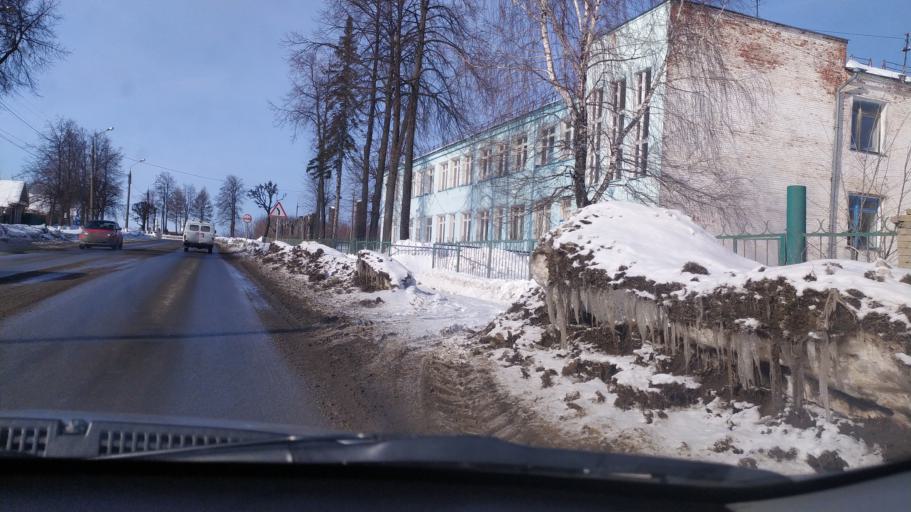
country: RU
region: Chuvashia
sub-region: Cheboksarskiy Rayon
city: Cheboksary
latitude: 56.1528
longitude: 47.2415
